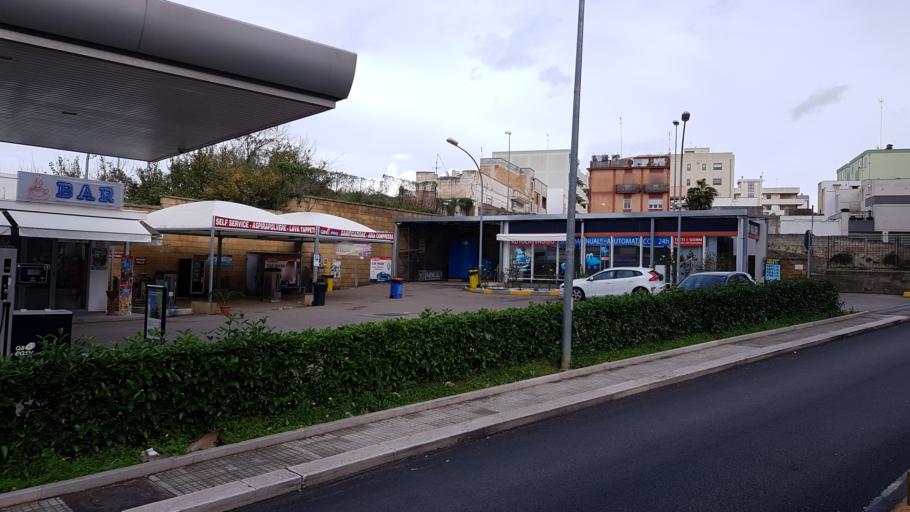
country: IT
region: Apulia
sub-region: Provincia di Brindisi
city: Brindisi
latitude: 40.6378
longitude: 17.9287
